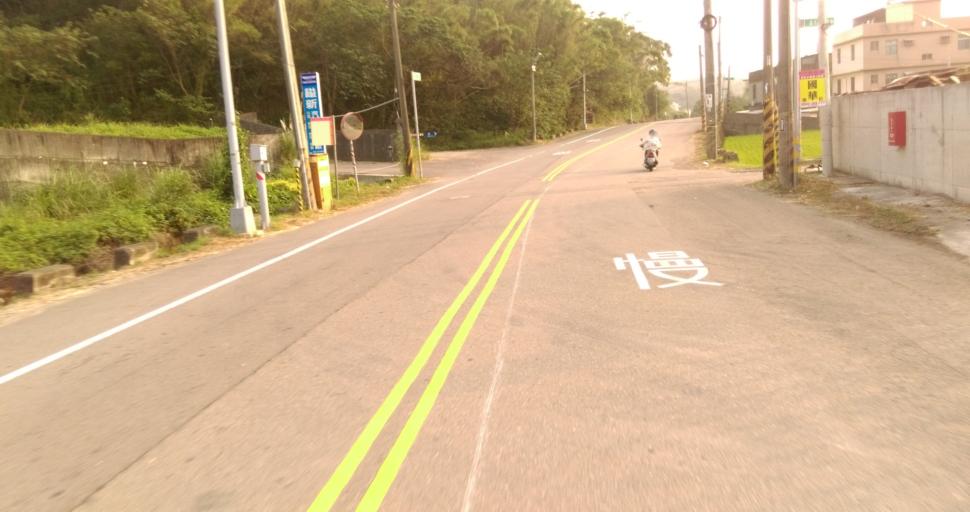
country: TW
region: Taiwan
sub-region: Hsinchu
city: Hsinchu
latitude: 24.7508
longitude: 120.9381
